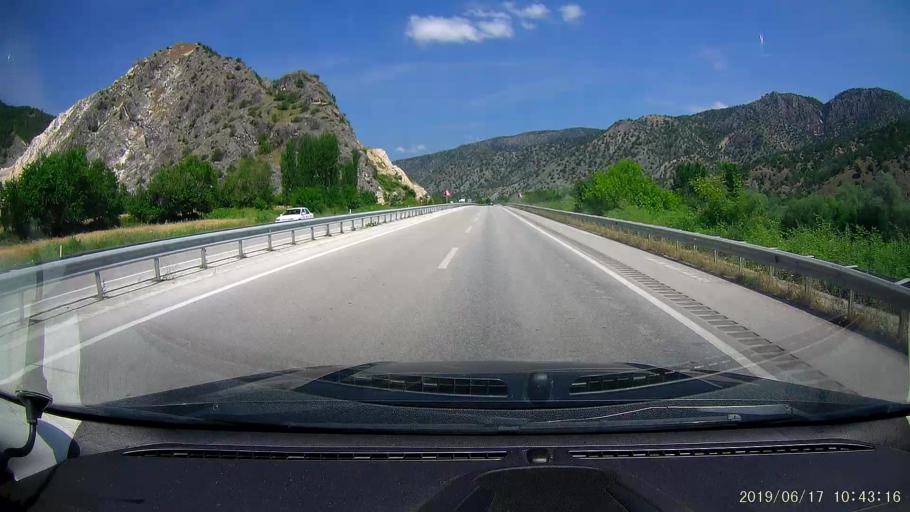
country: TR
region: Corum
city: Kargi
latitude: 41.0616
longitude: 34.5387
